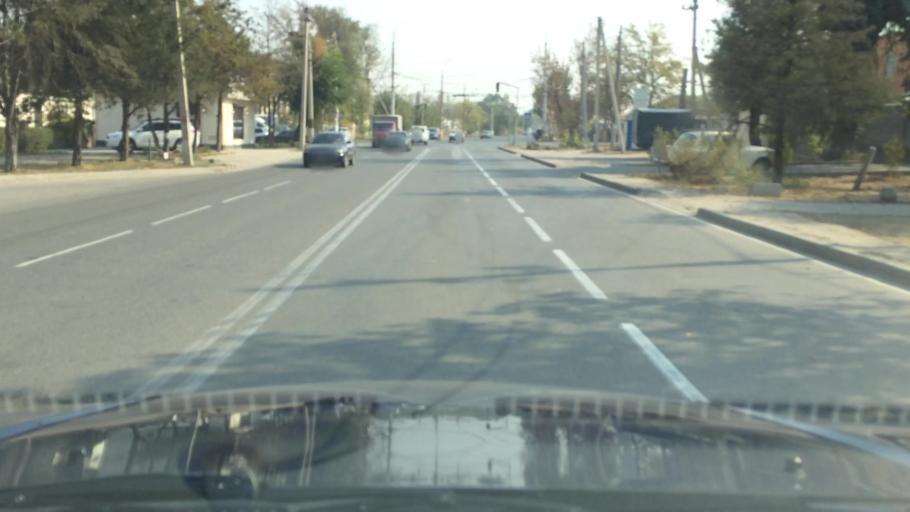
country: KG
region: Chuy
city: Lebedinovka
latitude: 42.8843
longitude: 74.6548
